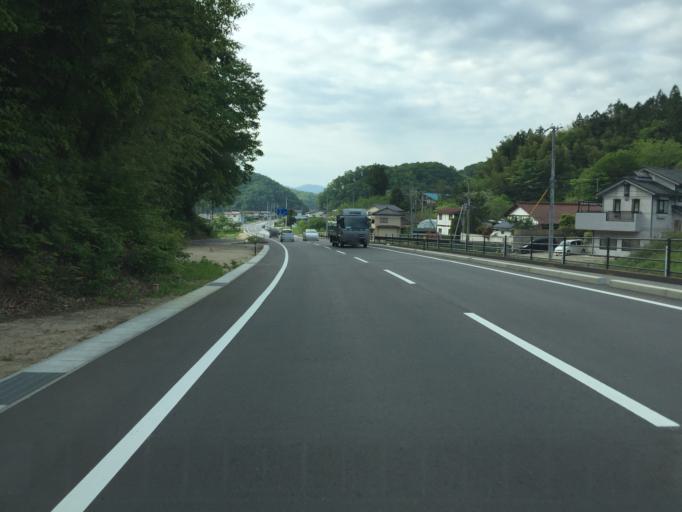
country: JP
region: Fukushima
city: Hobaramachi
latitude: 37.7333
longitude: 140.6034
